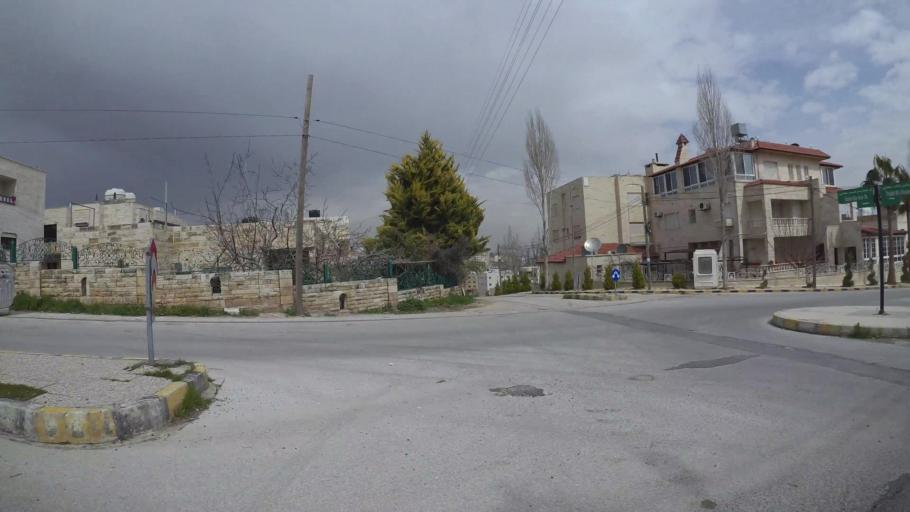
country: JO
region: Amman
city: Umm as Summaq
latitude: 31.9058
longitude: 35.8460
